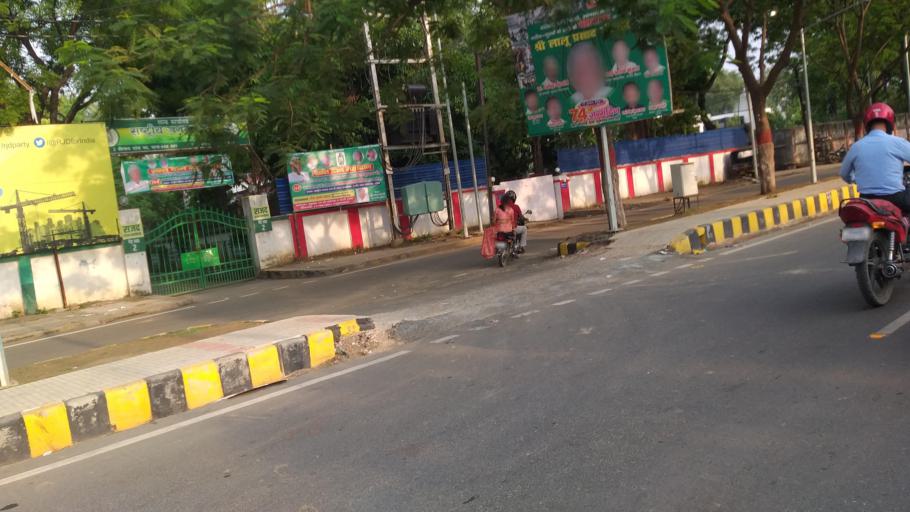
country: IN
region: Bihar
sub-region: Patna
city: Patna
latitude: 25.6054
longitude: 85.1282
